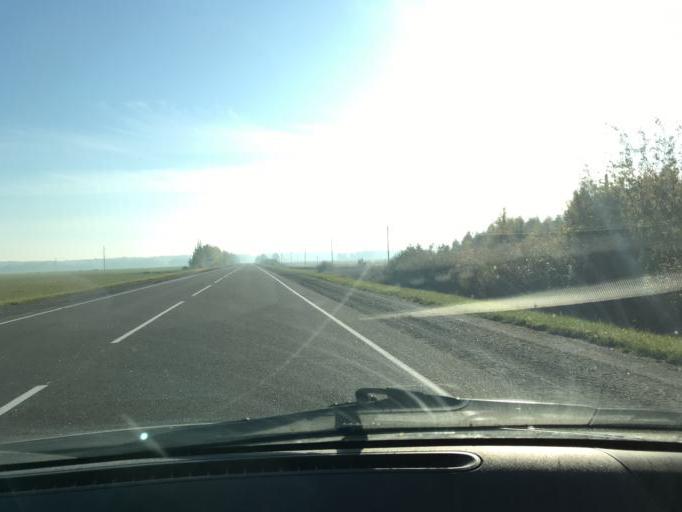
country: BY
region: Brest
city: Horad Luninyets
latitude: 52.3141
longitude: 26.6490
